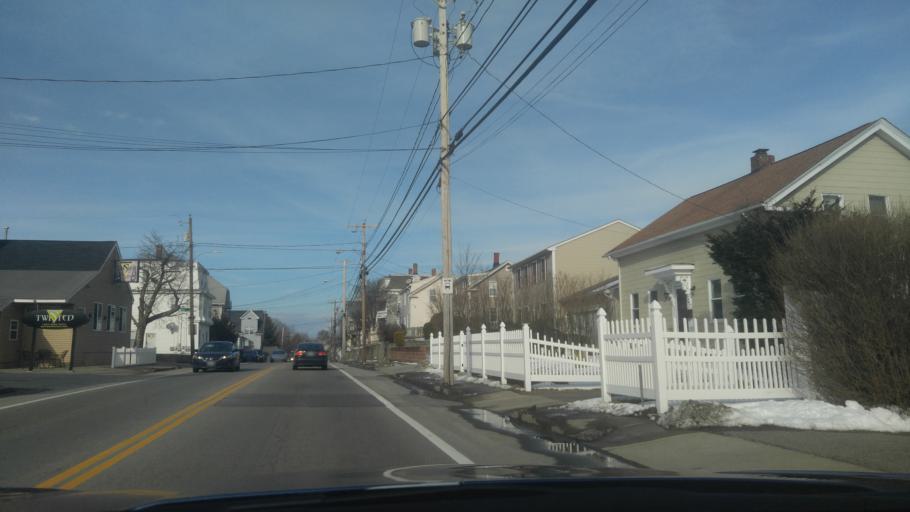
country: US
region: Rhode Island
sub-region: Kent County
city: West Warwick
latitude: 41.7157
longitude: -71.4949
